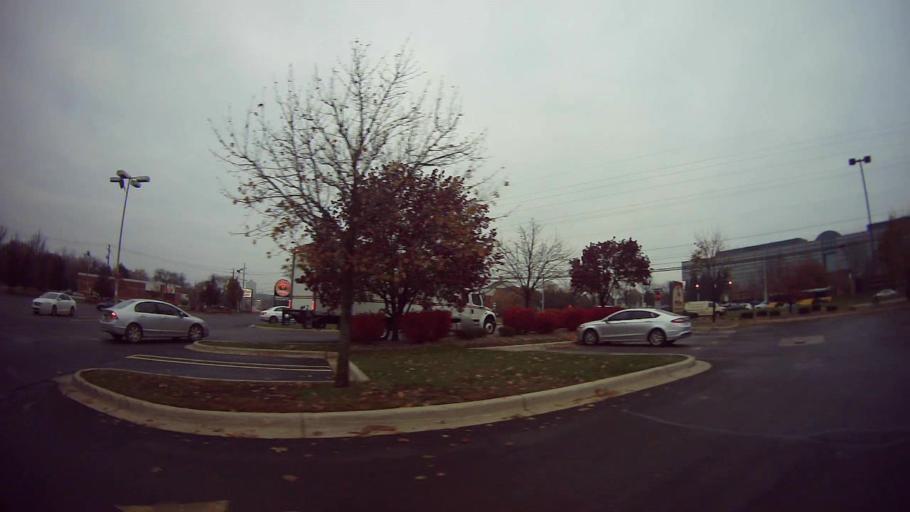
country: US
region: Michigan
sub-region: Oakland County
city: Bingham Farms
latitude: 42.4739
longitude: -83.2839
